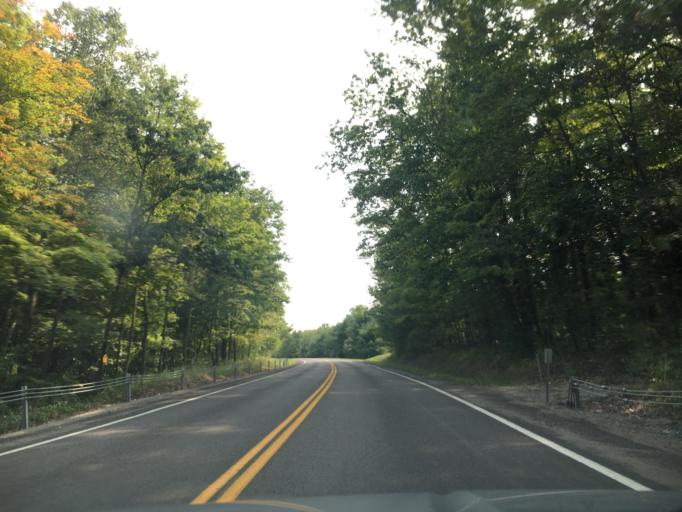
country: US
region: New York
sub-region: Steuben County
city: Sylvan Beach
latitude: 42.4798
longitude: -77.1250
